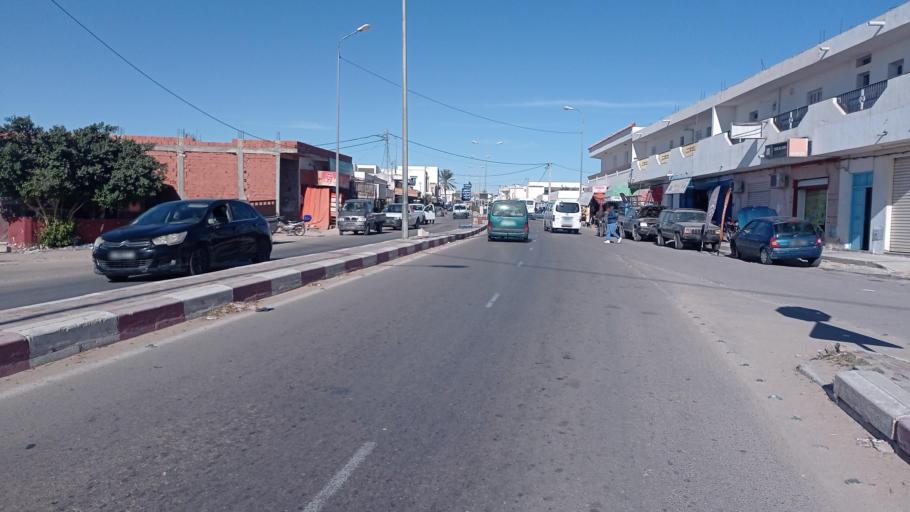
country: TN
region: Qabis
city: Gabes
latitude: 33.8391
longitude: 10.1159
